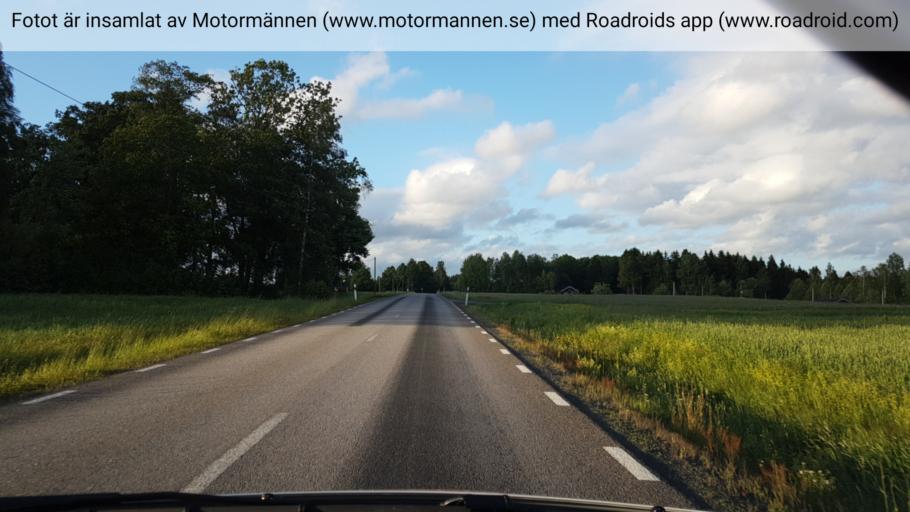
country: SE
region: OErebro
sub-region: Karlskoga Kommun
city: Karlskoga
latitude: 59.3884
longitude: 14.6115
